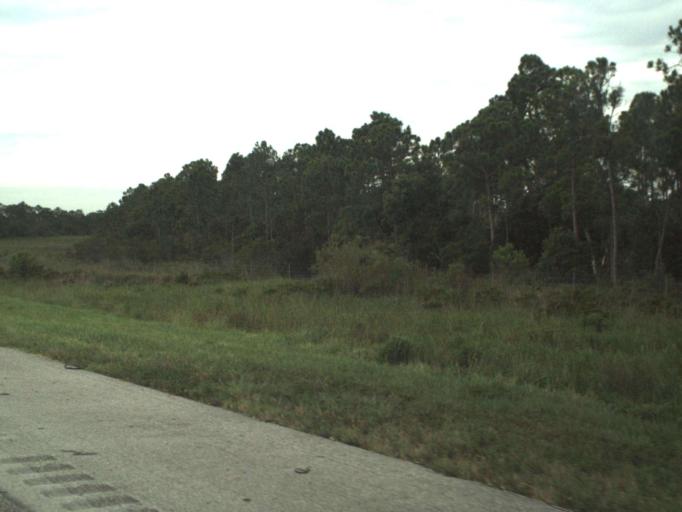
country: US
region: Florida
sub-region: Martin County
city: Palm City
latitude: 27.1362
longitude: -80.3617
